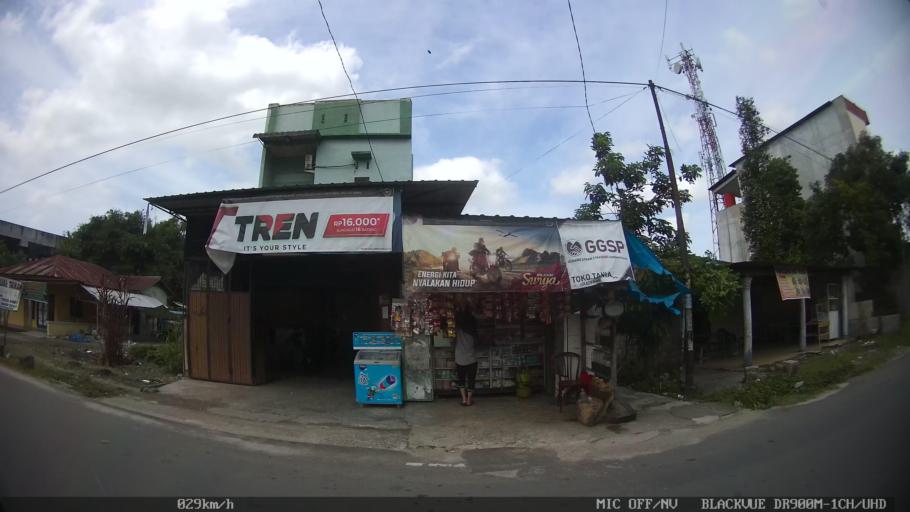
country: ID
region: North Sumatra
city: Percut
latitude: 3.6077
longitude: 98.8528
